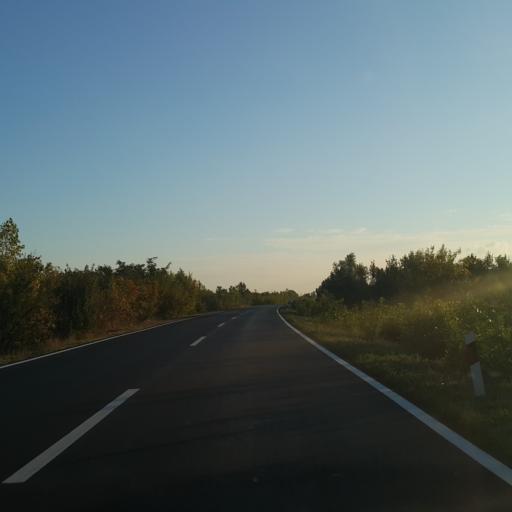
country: RS
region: Central Serbia
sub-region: Borski Okrug
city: Negotin
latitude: 44.1974
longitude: 22.3736
